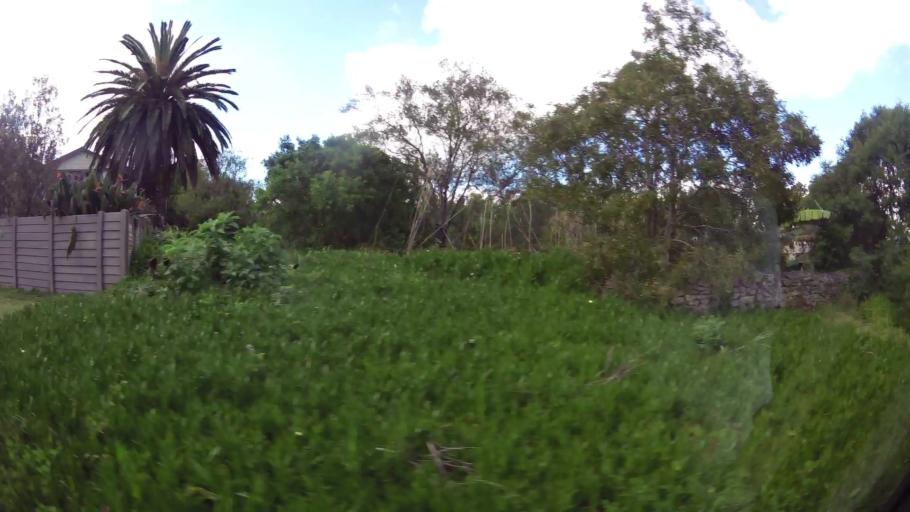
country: ZA
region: Western Cape
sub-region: Eden District Municipality
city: Knysna
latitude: -34.0445
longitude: 23.0728
